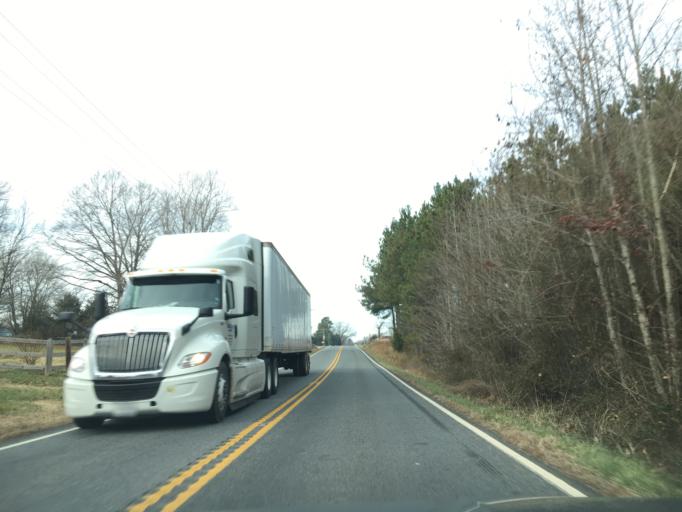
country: US
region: Virginia
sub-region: Goochland County
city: Goochland
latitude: 37.8278
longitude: -77.8937
